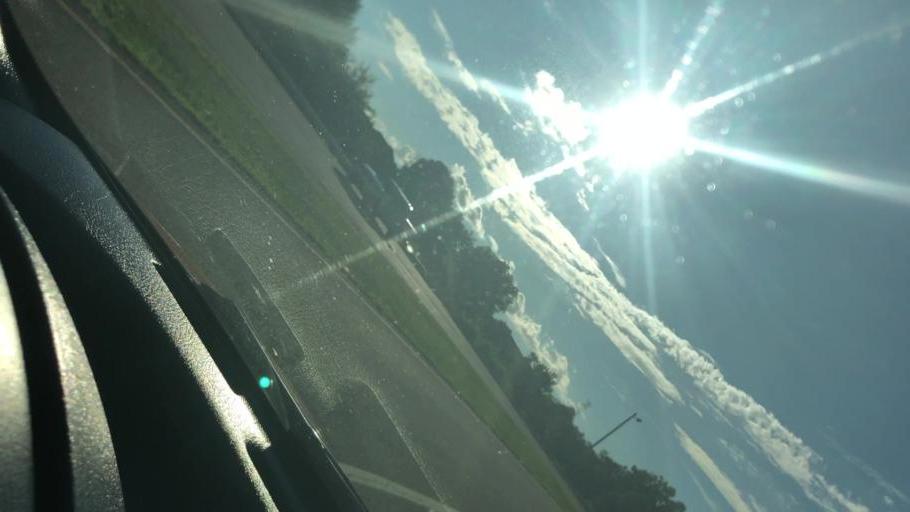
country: US
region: Tennessee
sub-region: Jefferson County
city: Jefferson City
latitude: 36.0603
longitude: -83.4748
